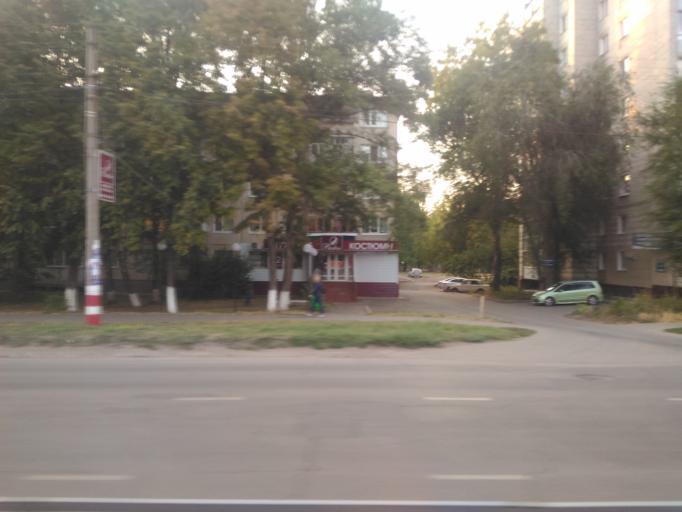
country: RU
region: Ulyanovsk
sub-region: Ulyanovskiy Rayon
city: Ulyanovsk
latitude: 54.2829
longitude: 48.2991
